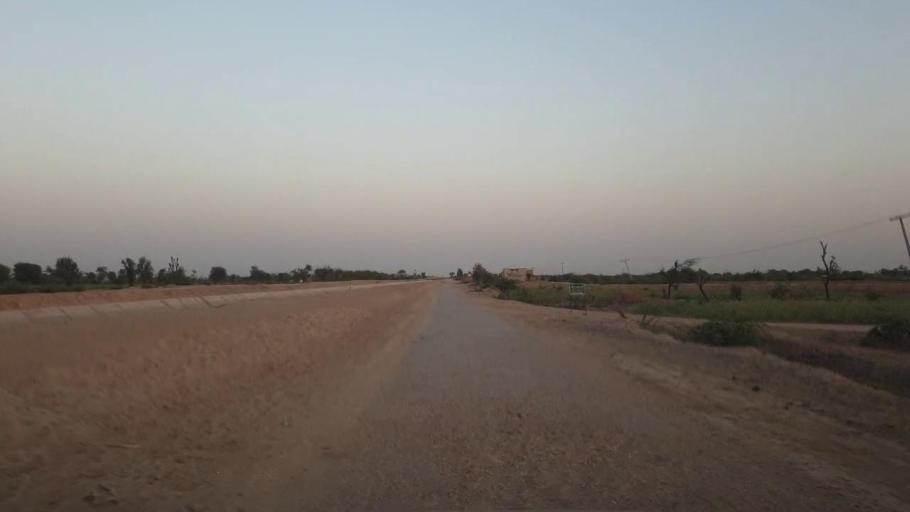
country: PK
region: Sindh
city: Dhoro Naro
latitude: 25.4358
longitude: 69.6441
